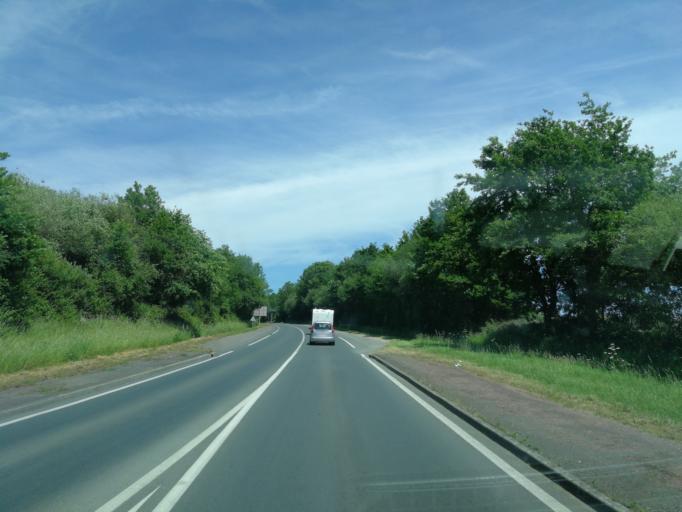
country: FR
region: Pays de la Loire
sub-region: Departement de la Vendee
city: La Chataigneraie
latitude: 46.6421
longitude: -0.7281
